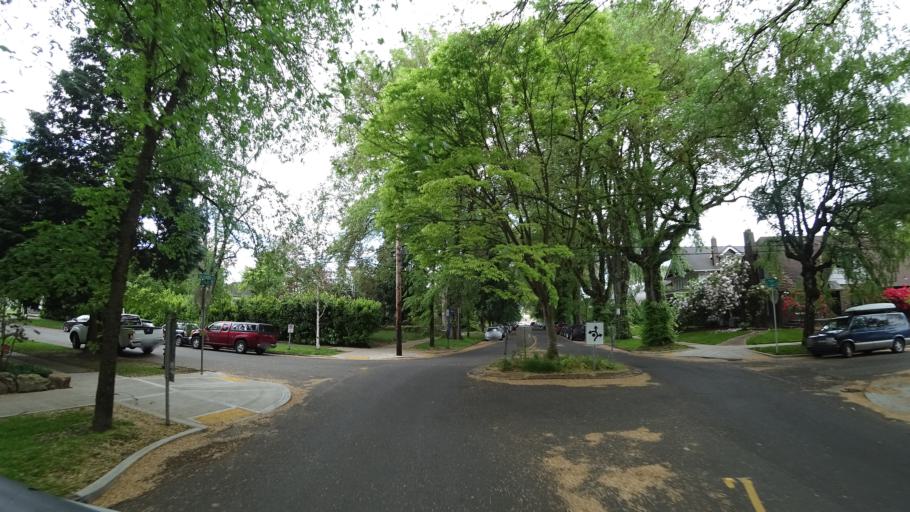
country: US
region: Oregon
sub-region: Multnomah County
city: Portland
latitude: 45.5102
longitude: -122.6514
